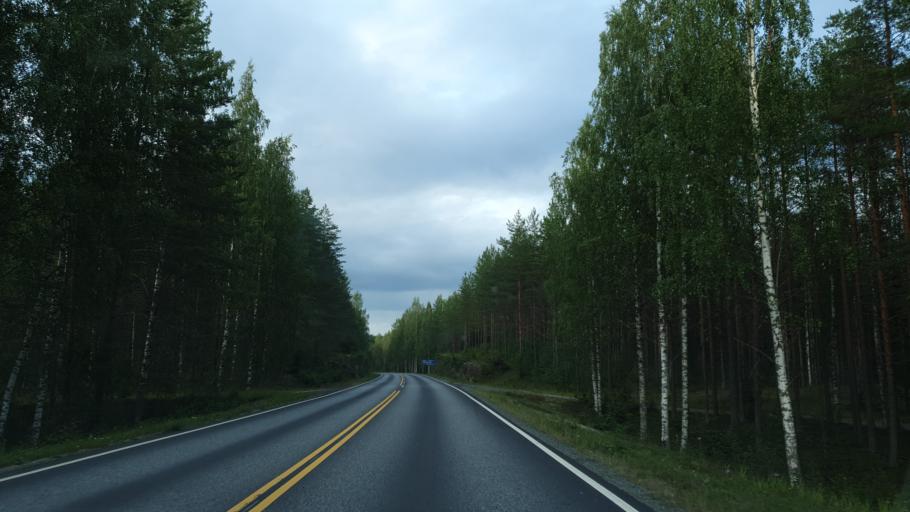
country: FI
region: North Karelia
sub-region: Joensuu
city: Eno
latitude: 63.0396
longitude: 30.1181
